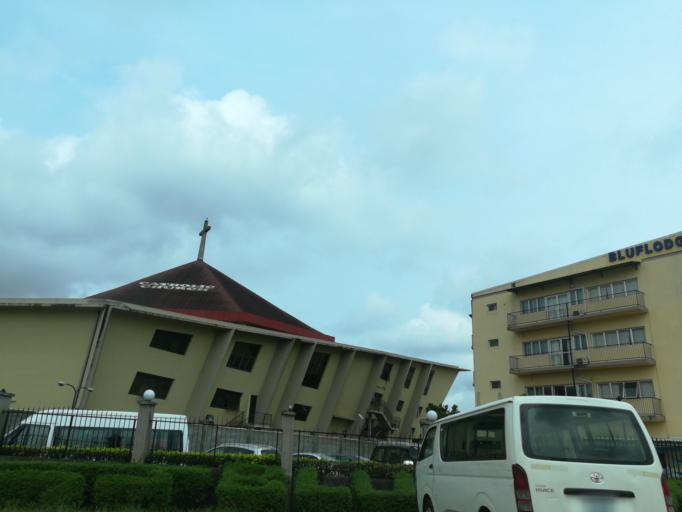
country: NG
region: Lagos
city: Oshodi
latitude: 6.5712
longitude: 3.3235
